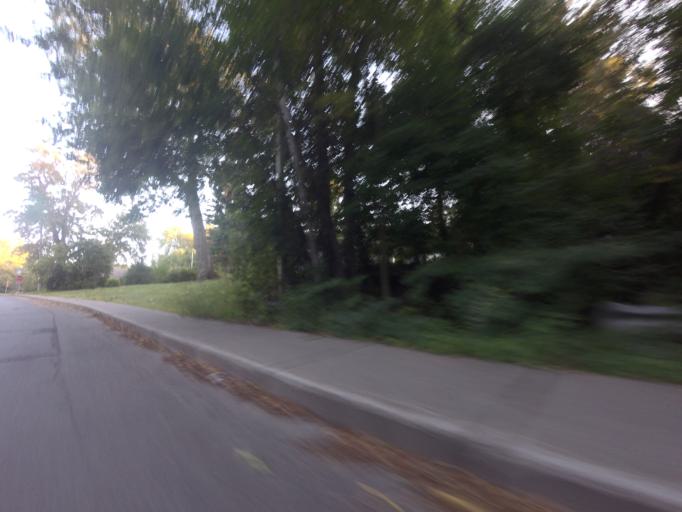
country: CA
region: Quebec
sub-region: Monteregie
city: Hudson
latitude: 45.4550
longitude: -74.1362
